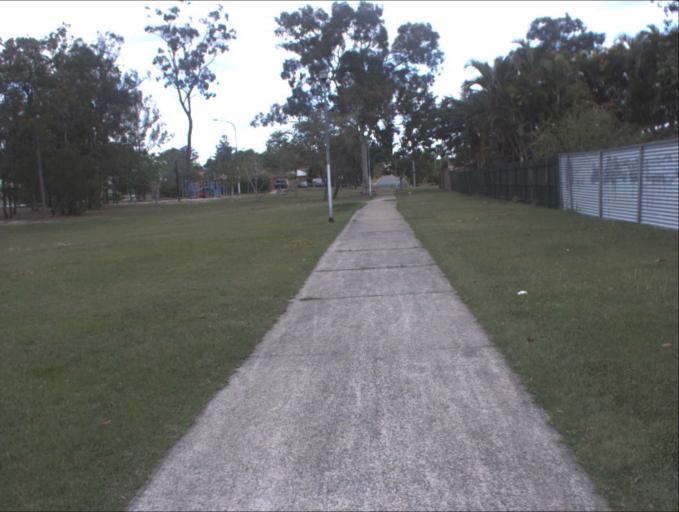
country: AU
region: Queensland
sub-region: Logan
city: Waterford West
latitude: -27.6773
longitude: 153.0979
